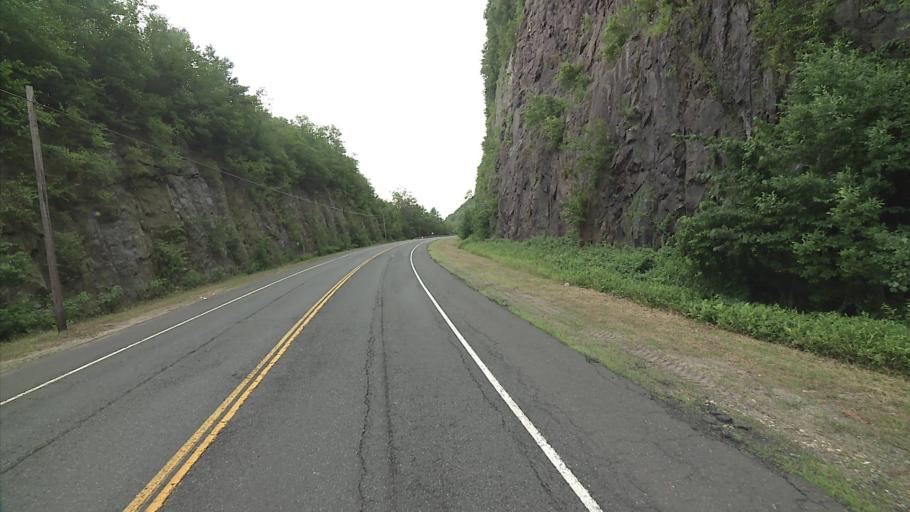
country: US
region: Connecticut
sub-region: Litchfield County
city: Winsted
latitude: 42.0130
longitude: -73.0494
